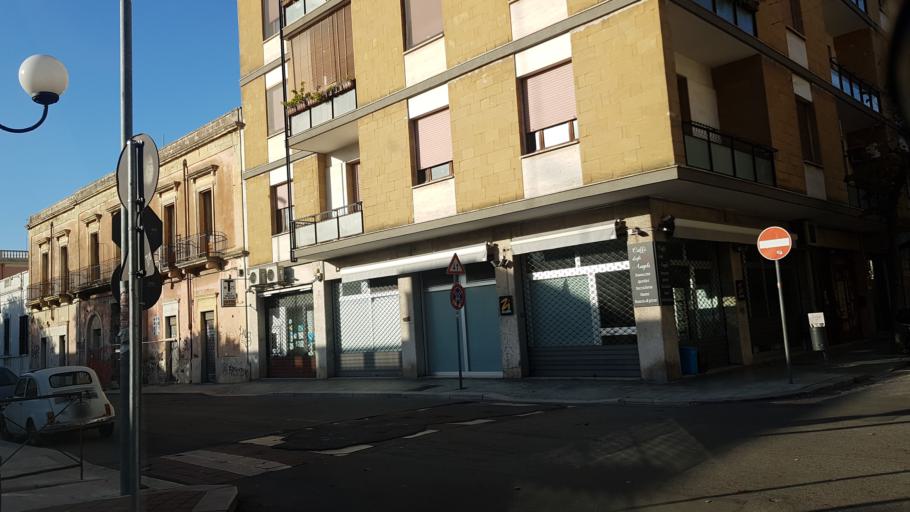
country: IT
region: Apulia
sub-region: Provincia di Lecce
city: Lecce
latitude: 40.3517
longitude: 18.1611
